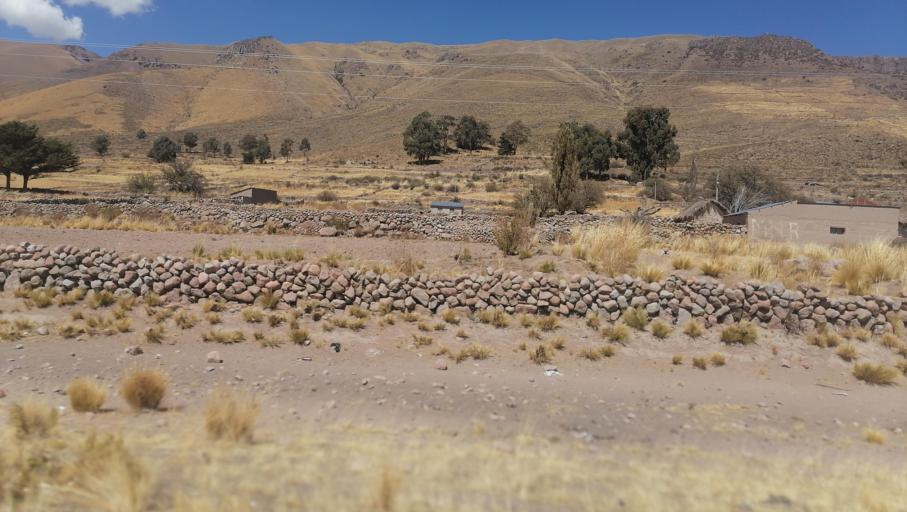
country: BO
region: Oruro
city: Challapata
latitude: -18.9917
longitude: -66.7784
